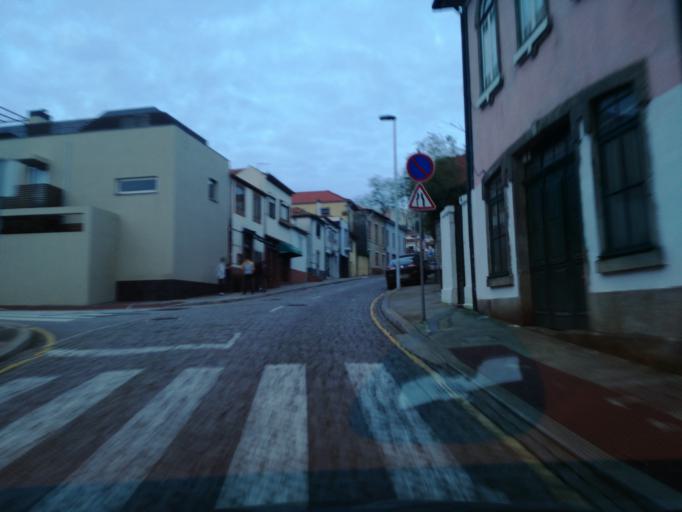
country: PT
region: Porto
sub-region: Vila Nova de Gaia
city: Canidelo
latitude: 41.1496
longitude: -8.6526
